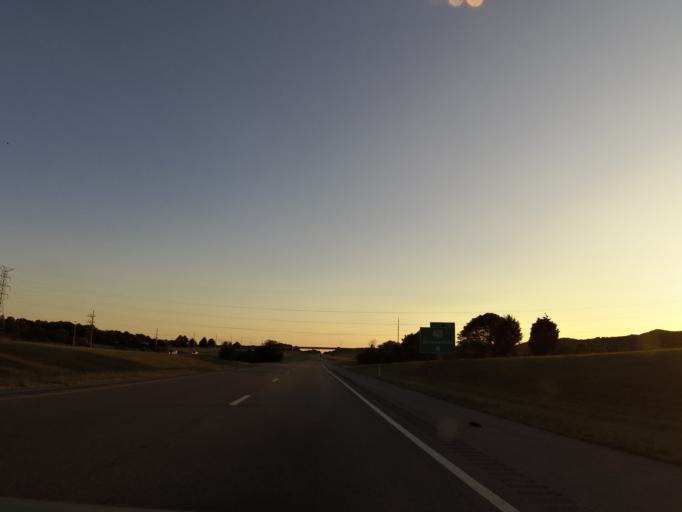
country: US
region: Tennessee
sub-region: Greene County
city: Mosheim
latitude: 36.2776
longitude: -82.9154
